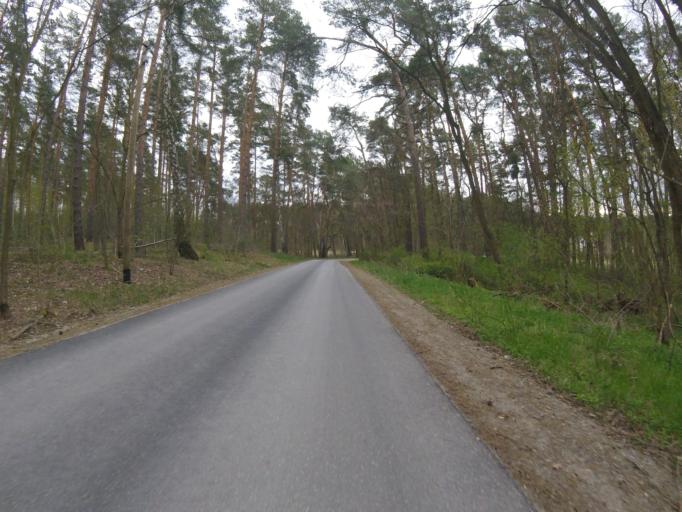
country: DE
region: Brandenburg
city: Schwerin
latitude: 52.1494
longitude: 13.6457
